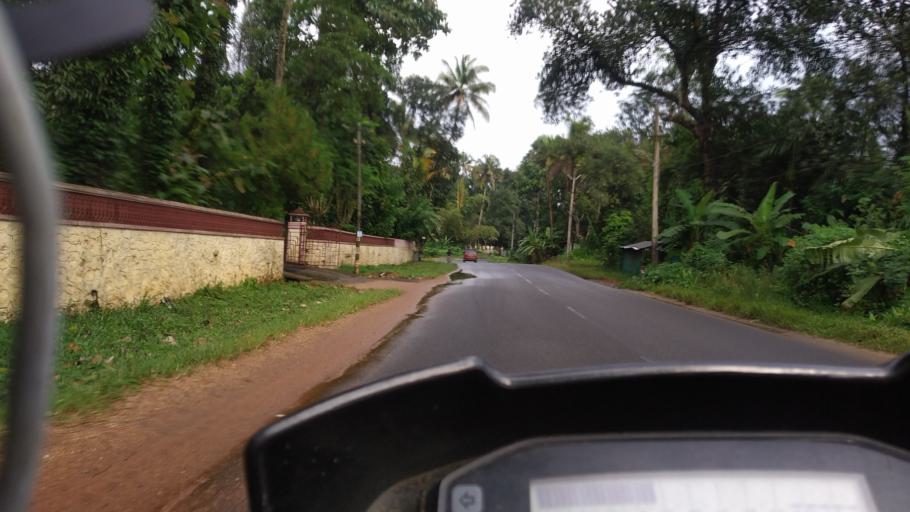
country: IN
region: Kerala
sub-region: Ernakulam
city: Kotamangalam
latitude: 10.0587
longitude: 76.6913
